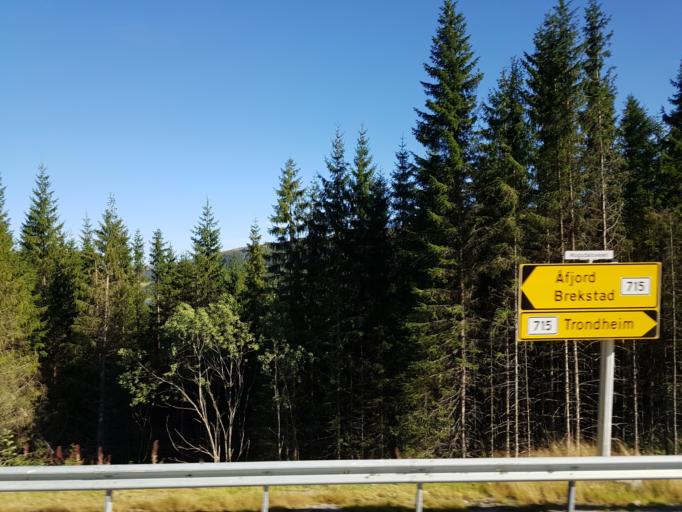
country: NO
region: Sor-Trondelag
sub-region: Afjord
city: A i Afjord
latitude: 63.7796
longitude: 10.2178
